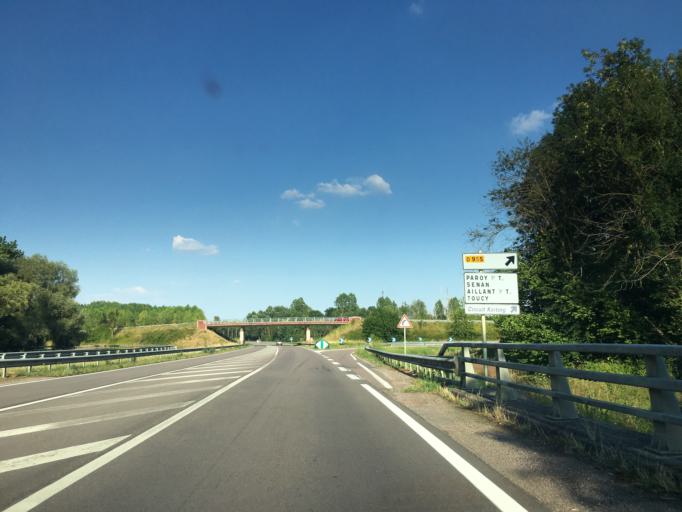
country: FR
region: Bourgogne
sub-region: Departement de l'Yonne
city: Joigny
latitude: 47.9654
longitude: 3.3823
